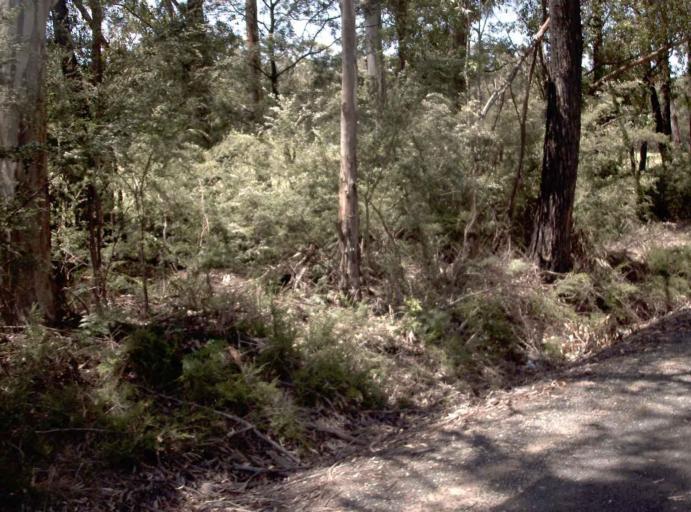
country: AU
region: Victoria
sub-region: East Gippsland
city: Lakes Entrance
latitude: -37.7402
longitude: 148.1550
